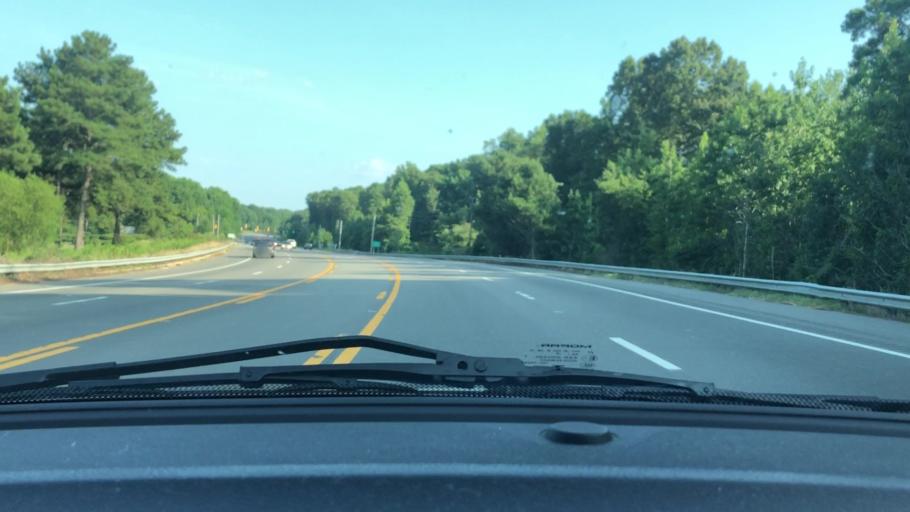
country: US
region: North Carolina
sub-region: Lee County
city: Broadway
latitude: 35.4015
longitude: -79.1138
